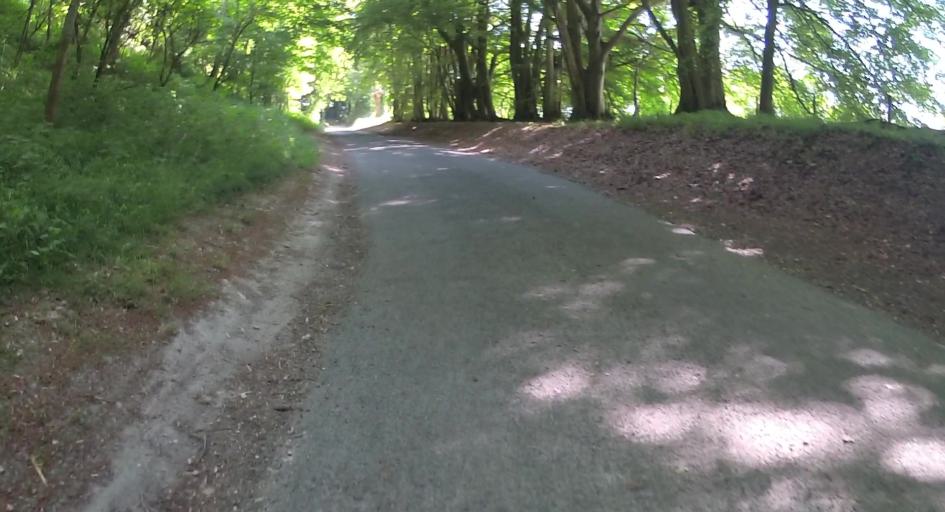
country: GB
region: England
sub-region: Hampshire
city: Kingsclere
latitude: 51.3083
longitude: -1.2960
